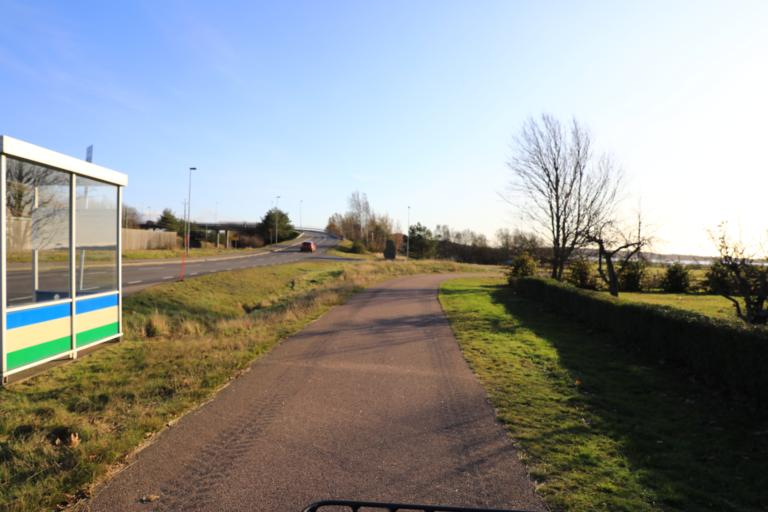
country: SE
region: Halland
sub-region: Varbergs Kommun
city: Varberg
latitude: 57.1717
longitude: 12.2280
